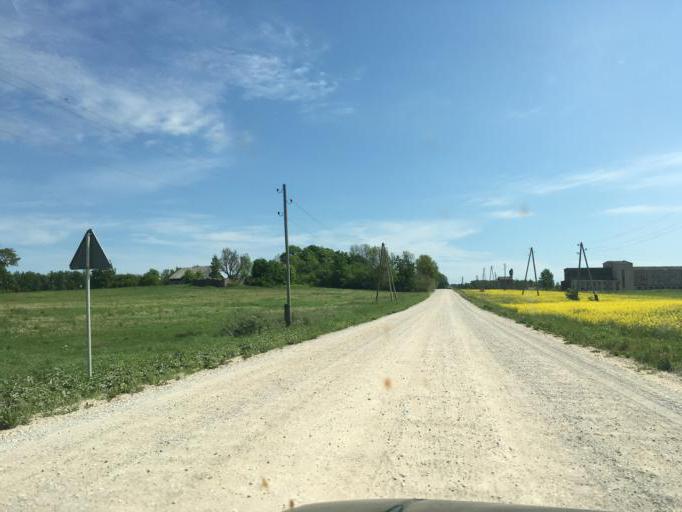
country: LV
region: Talsu Rajons
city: Valdemarpils
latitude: 57.3766
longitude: 22.6136
